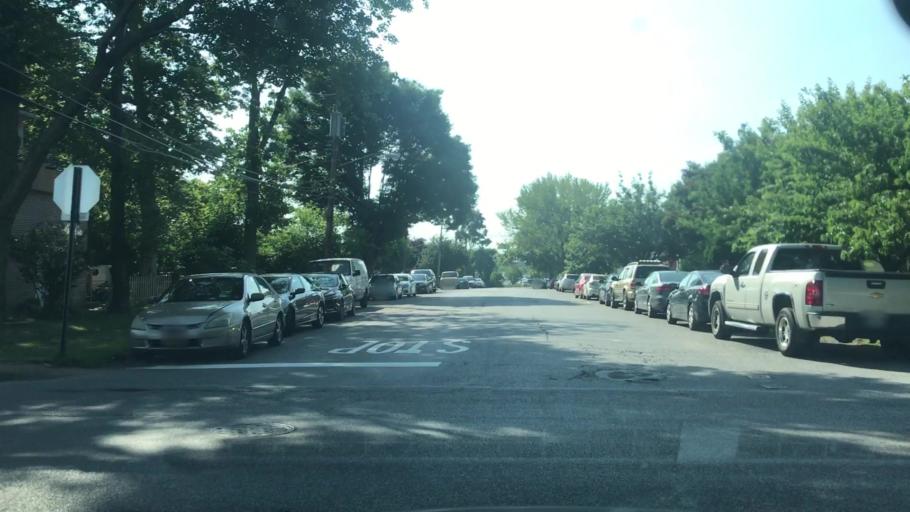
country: US
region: New York
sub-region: Richmond County
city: Staten Island
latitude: 40.5882
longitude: -74.0882
